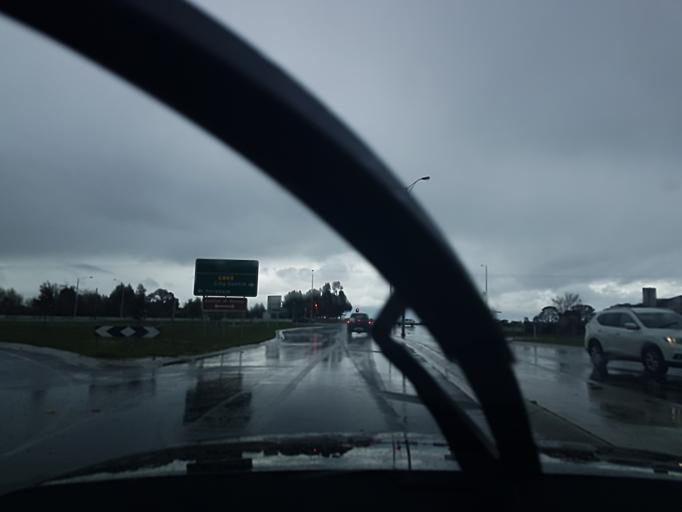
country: AU
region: Victoria
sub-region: Ballarat North
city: Newington
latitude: -37.5434
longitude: 143.7868
